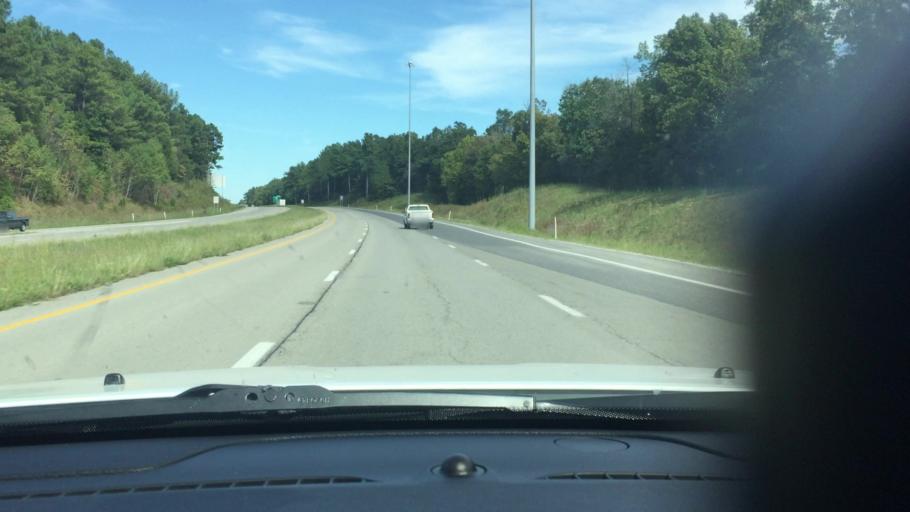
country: US
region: Kentucky
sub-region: Caldwell County
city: Princeton
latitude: 37.1236
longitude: -87.8895
